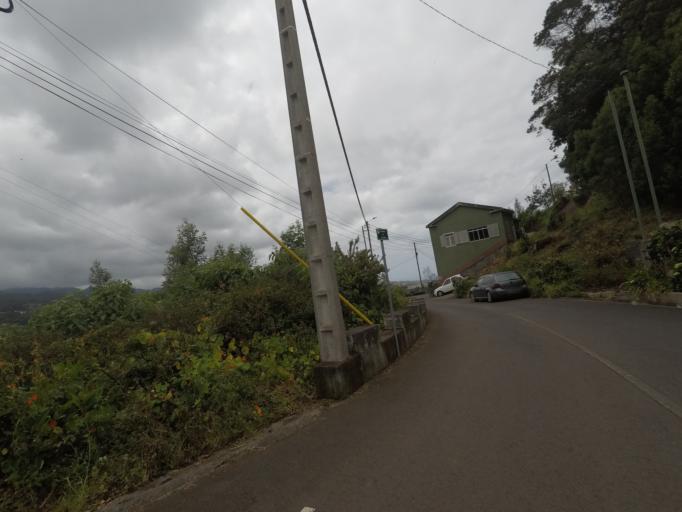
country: PT
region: Madeira
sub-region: Santana
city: Santana
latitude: 32.7965
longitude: -16.8661
